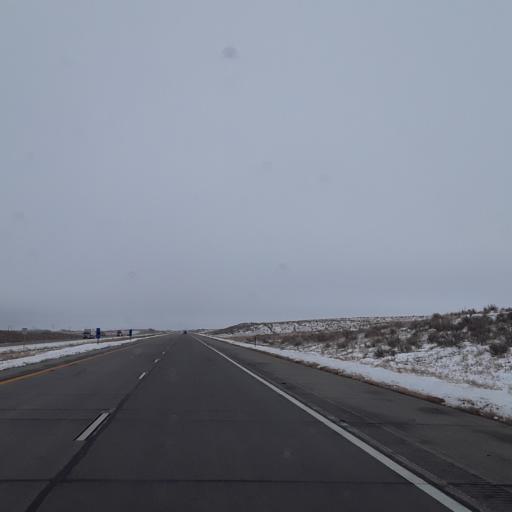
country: US
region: Colorado
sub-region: Logan County
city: Sterling
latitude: 40.5776
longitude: -103.1997
